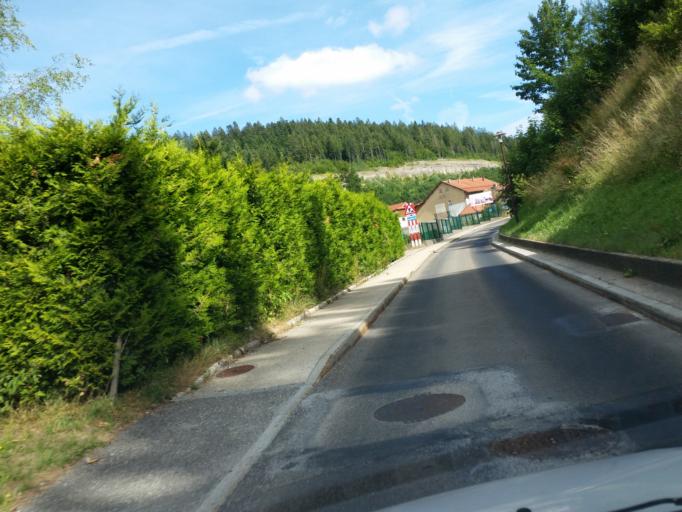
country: FR
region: Franche-Comte
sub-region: Departement du Doubs
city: Jougne
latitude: 46.7761
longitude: 6.3748
